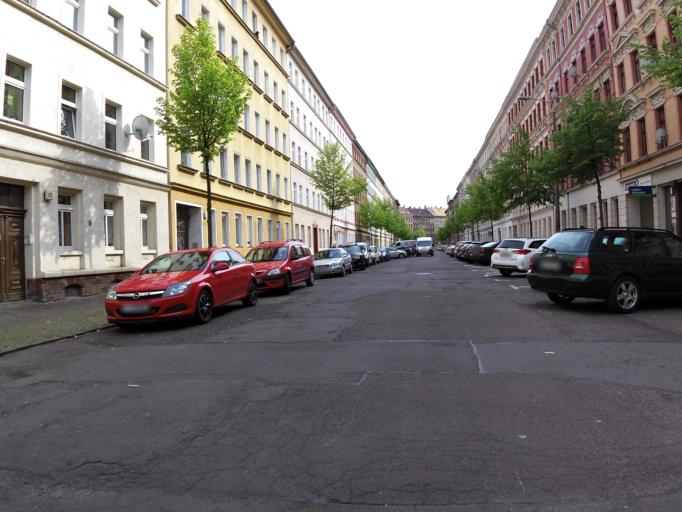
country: DE
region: Saxony
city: Leipzig
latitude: 51.3538
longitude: 12.4088
